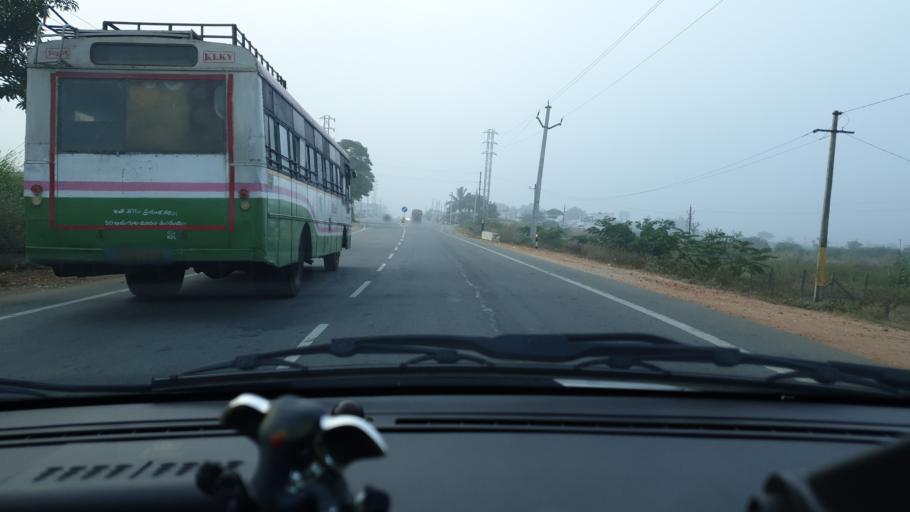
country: IN
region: Telangana
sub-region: Mahbubnagar
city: Farrukhnagar
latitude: 16.8864
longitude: 78.5290
